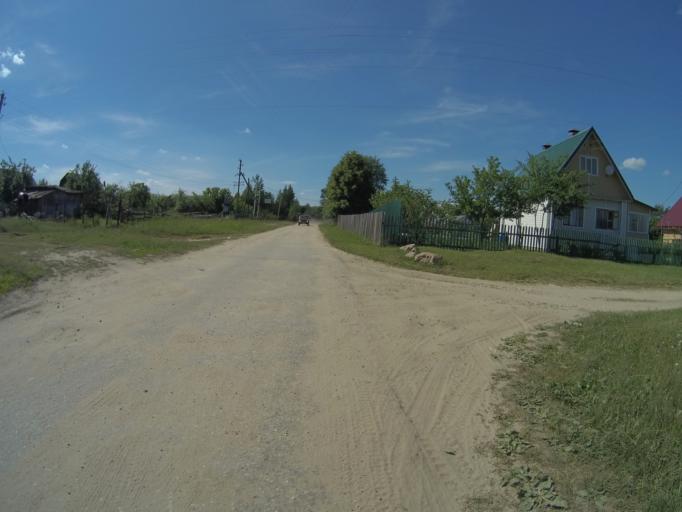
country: RU
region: Vladimir
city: Raduzhnyy
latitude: 55.9803
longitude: 40.3808
